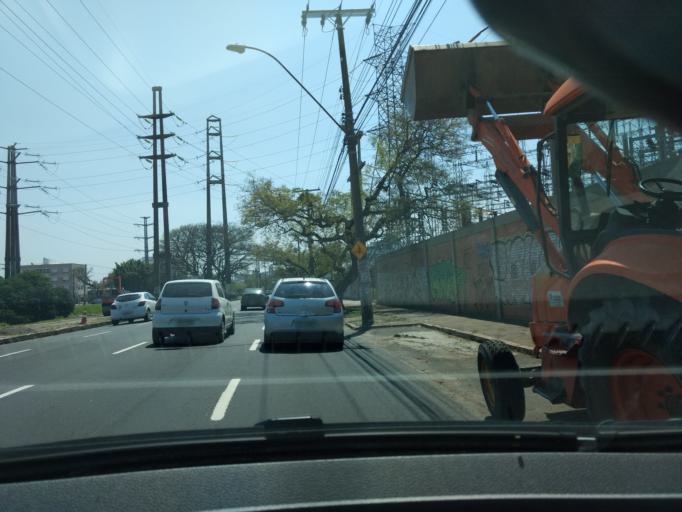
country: BR
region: Rio Grande do Sul
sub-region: Porto Alegre
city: Porto Alegre
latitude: -30.0479
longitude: -51.1964
